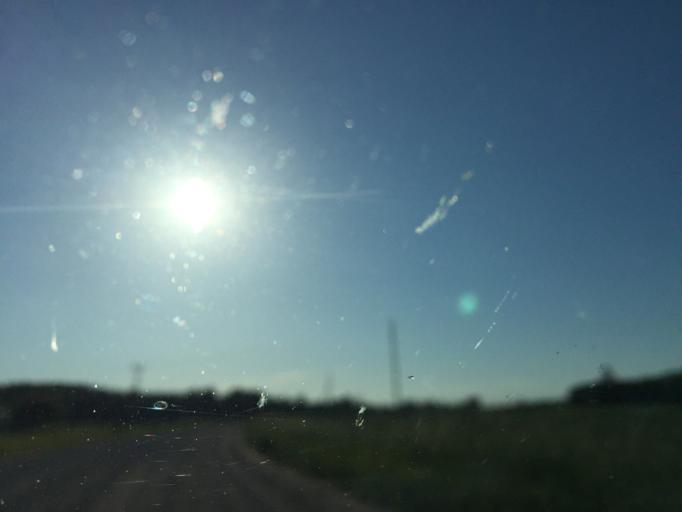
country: LV
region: Kandava
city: Kandava
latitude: 56.8351
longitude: 22.7240
